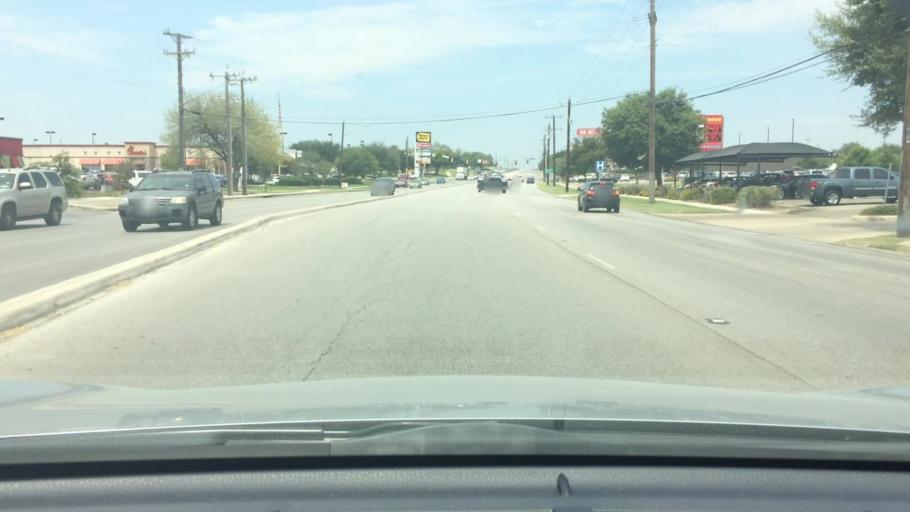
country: US
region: Texas
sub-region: Bexar County
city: China Grove
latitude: 29.3519
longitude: -98.4325
